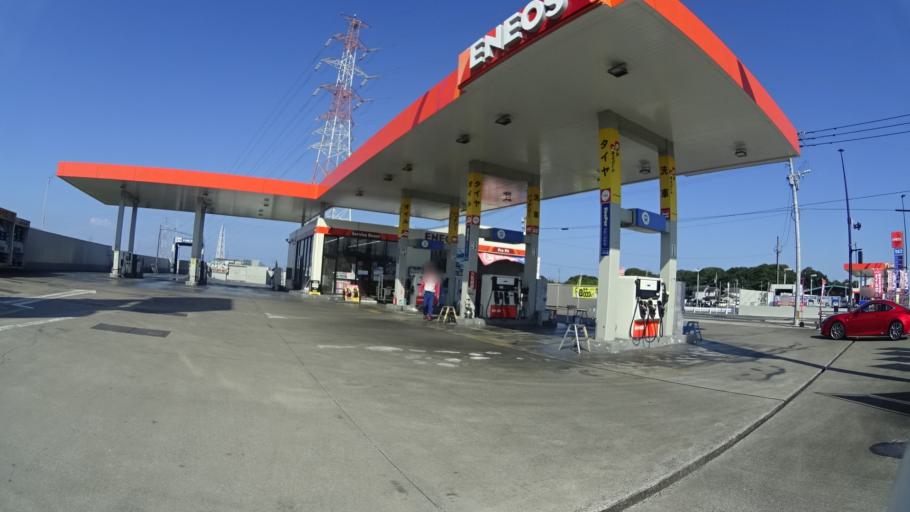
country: JP
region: Fukuoka
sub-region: Buzen-shi
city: Buzen
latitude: 33.6102
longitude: 131.1094
